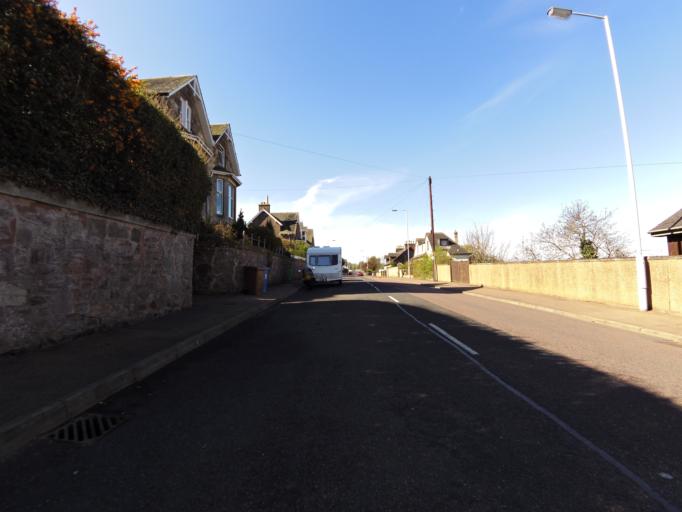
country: GB
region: Scotland
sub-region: Fife
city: Newport-On-Tay
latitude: 56.4272
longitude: -2.9739
